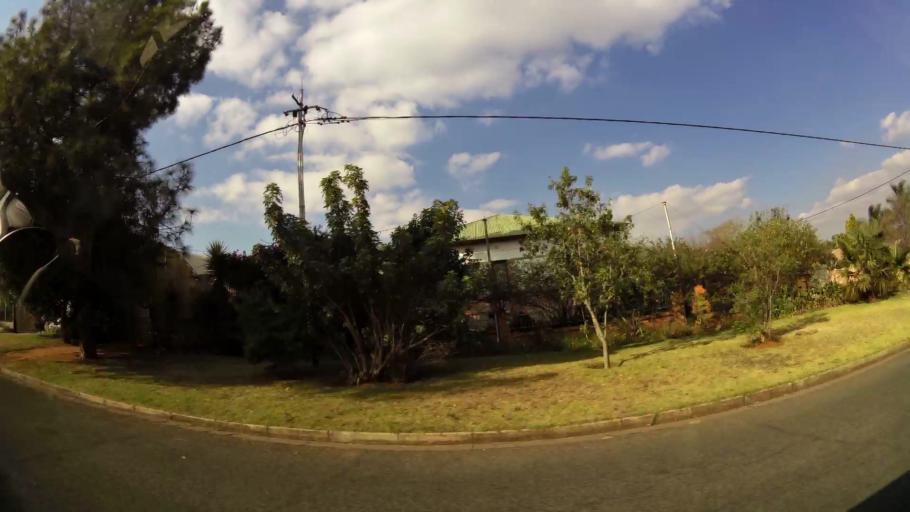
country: ZA
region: Gauteng
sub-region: West Rand District Municipality
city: Krugersdorp
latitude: -26.0866
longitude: 27.7652
